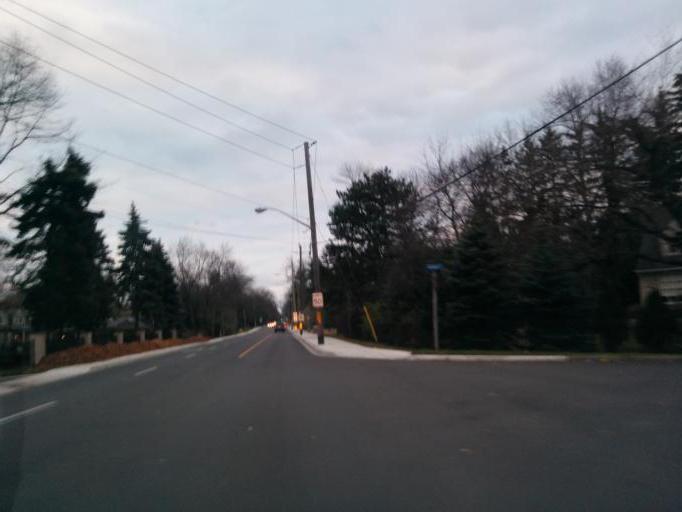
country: CA
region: Ontario
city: Mississauga
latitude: 43.5520
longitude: -79.6113
